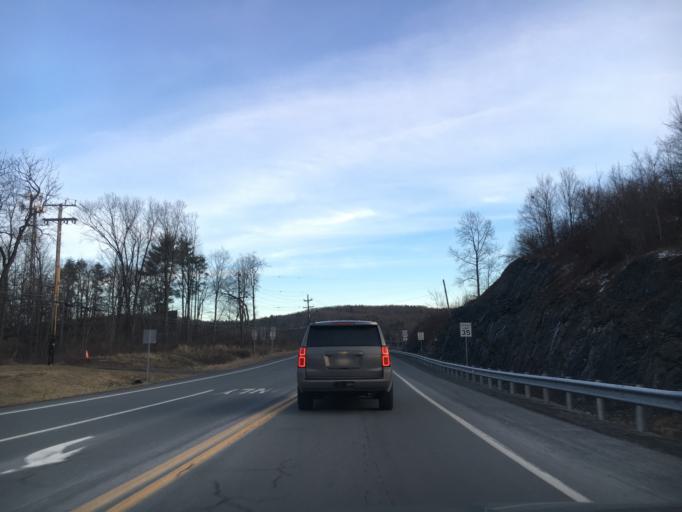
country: US
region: Pennsylvania
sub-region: Monroe County
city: East Stroudsburg
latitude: 41.0414
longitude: -75.1286
